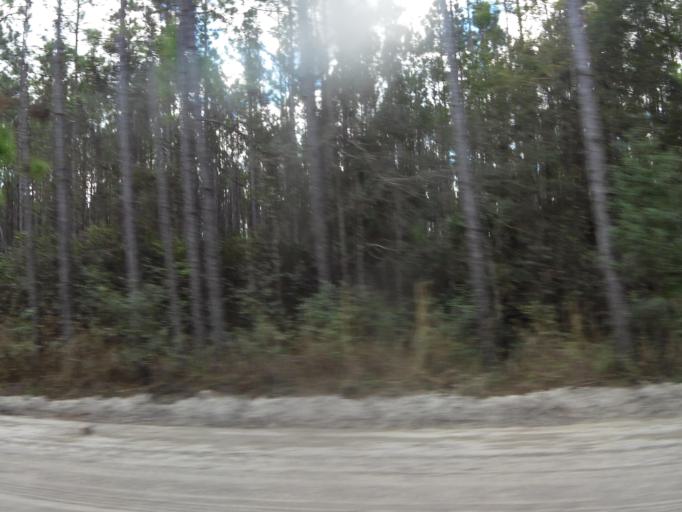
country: US
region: Florida
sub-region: Clay County
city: Green Cove Springs
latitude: 29.8370
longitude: -81.7538
